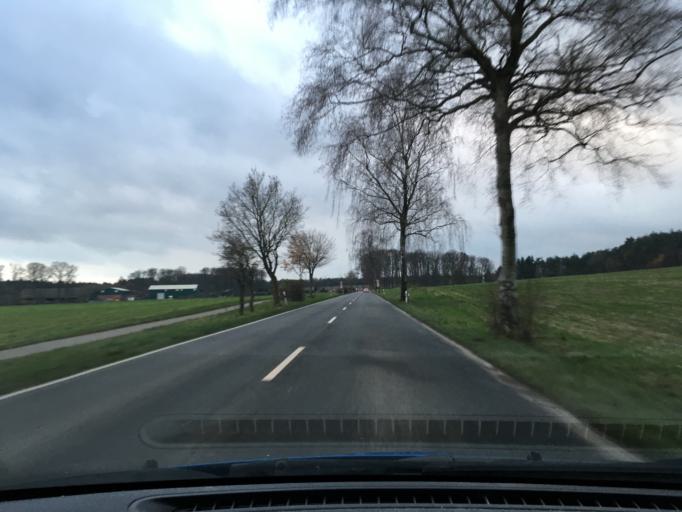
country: DE
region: Lower Saxony
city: Hermannsburg
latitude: 52.8672
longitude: 10.0923
